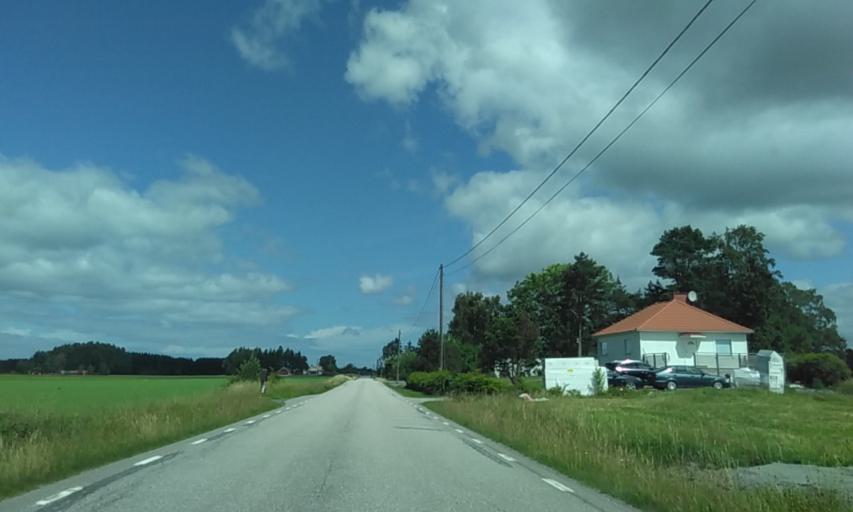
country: SE
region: Vaestra Goetaland
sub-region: Grastorps Kommun
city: Graestorp
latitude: 58.3647
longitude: 12.6828
